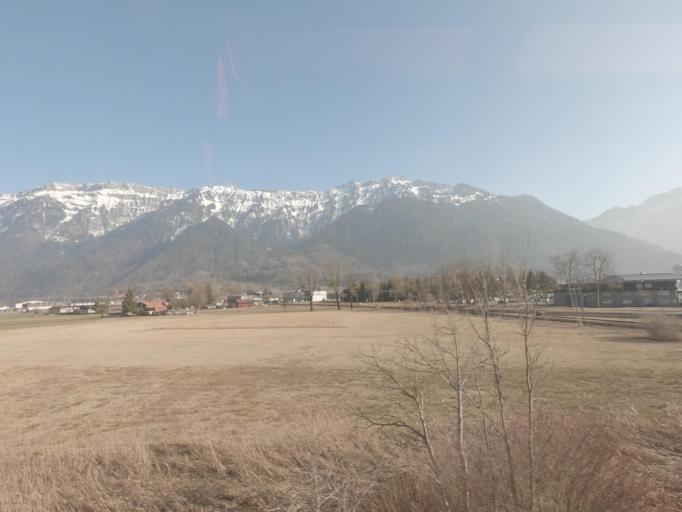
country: CH
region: Bern
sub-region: Interlaken-Oberhasli District
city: Interlaken
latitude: 46.6911
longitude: 7.8790
